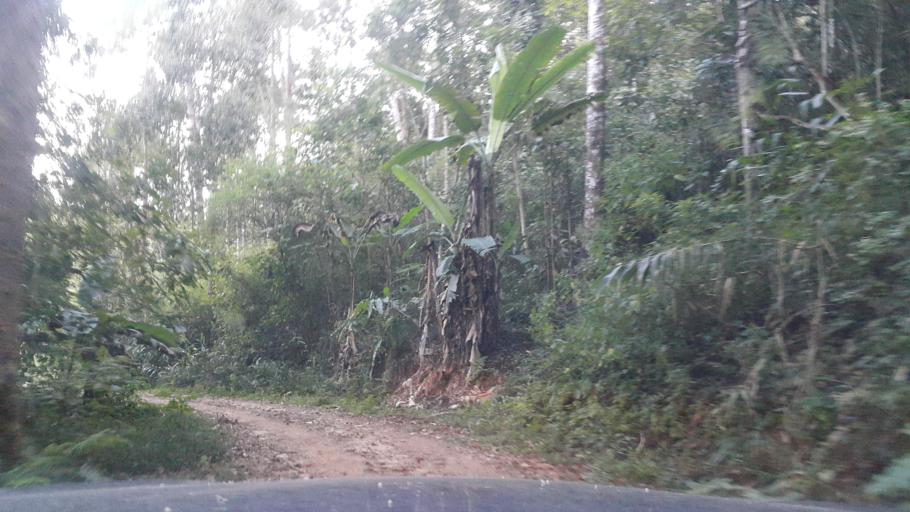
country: TH
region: Chiang Mai
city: Samoeng
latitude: 19.0160
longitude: 98.6490
